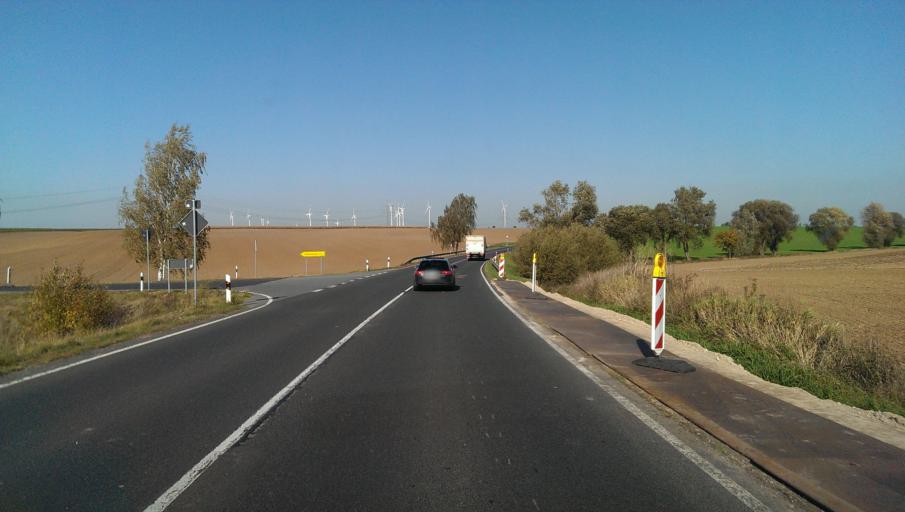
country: DE
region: Saxony
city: Ostrau
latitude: 51.2183
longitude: 13.1567
